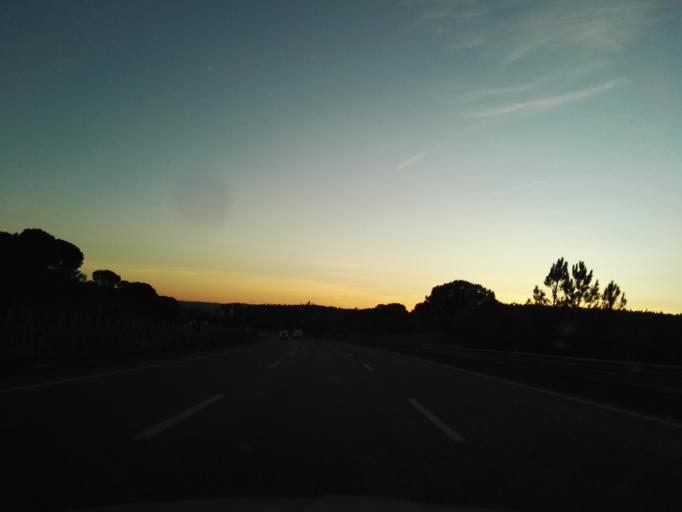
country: PT
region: Lisbon
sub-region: Azambuja
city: Aveiras de Cima
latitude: 39.1115
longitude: -8.9298
